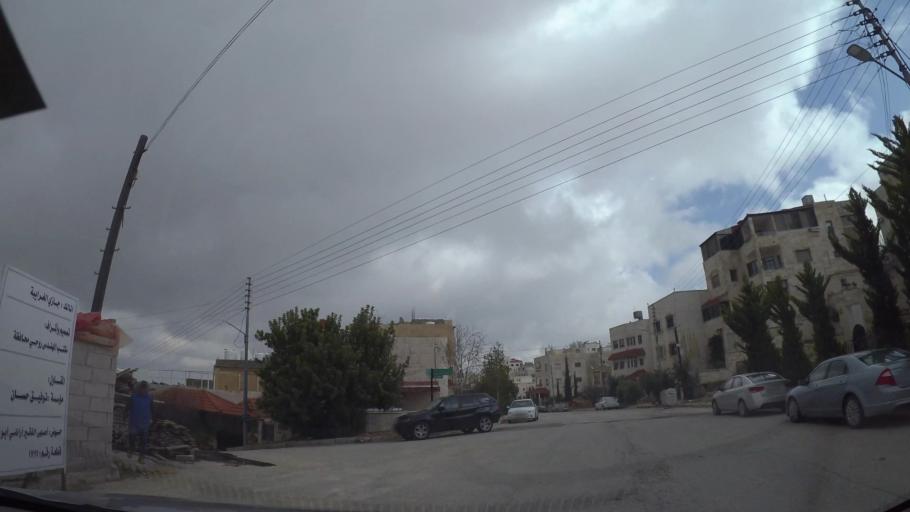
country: JO
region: Amman
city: Al Jubayhah
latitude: 32.0684
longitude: 35.8802
